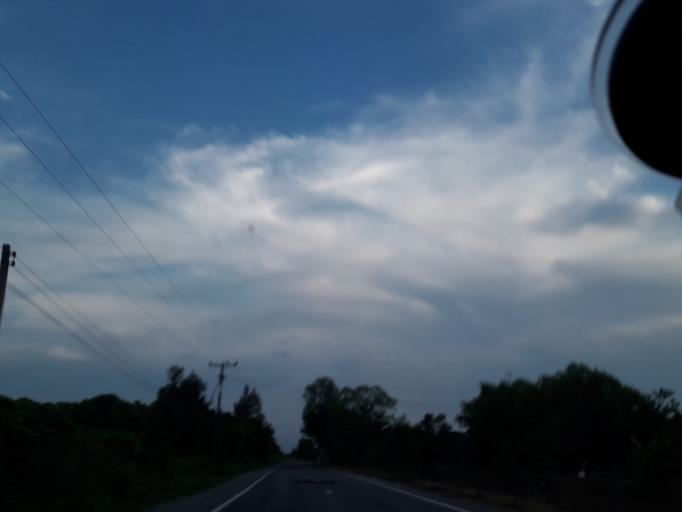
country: TH
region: Sara Buri
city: Nong Khae
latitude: 14.2582
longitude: 100.8688
